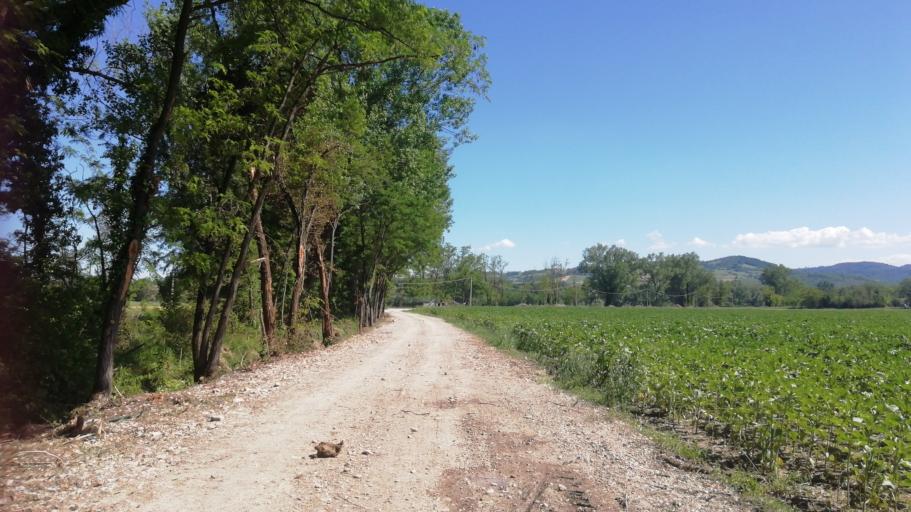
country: IT
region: Emilia-Romagna
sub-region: Provincia di Piacenza
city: Borgonovo Valtidone
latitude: 44.9865
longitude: 9.4582
